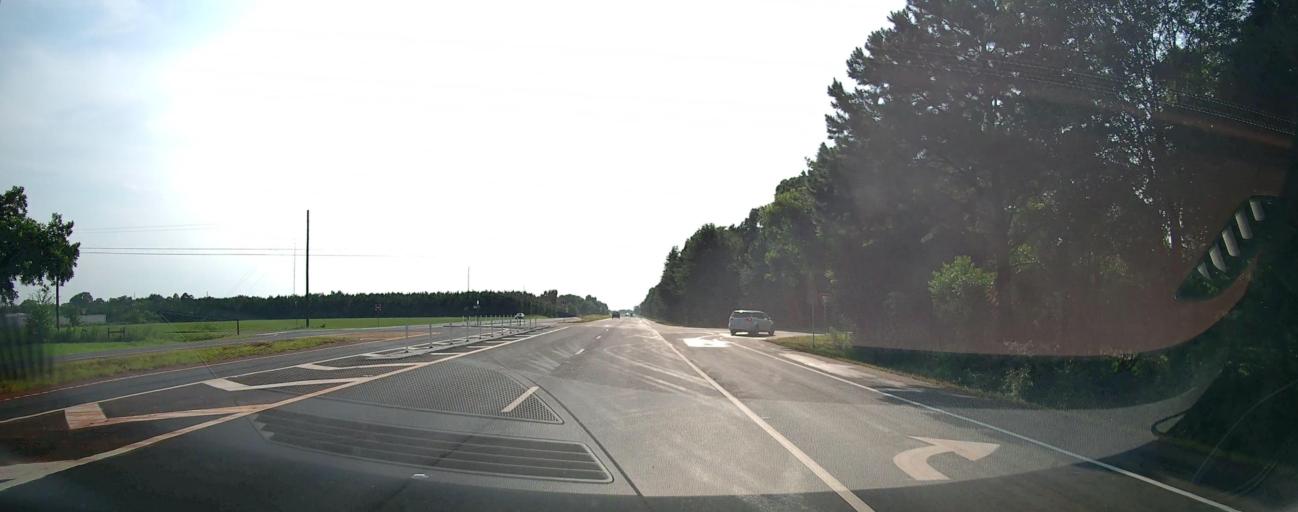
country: US
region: Georgia
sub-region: Peach County
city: Fort Valley
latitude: 32.5779
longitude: -83.8923
